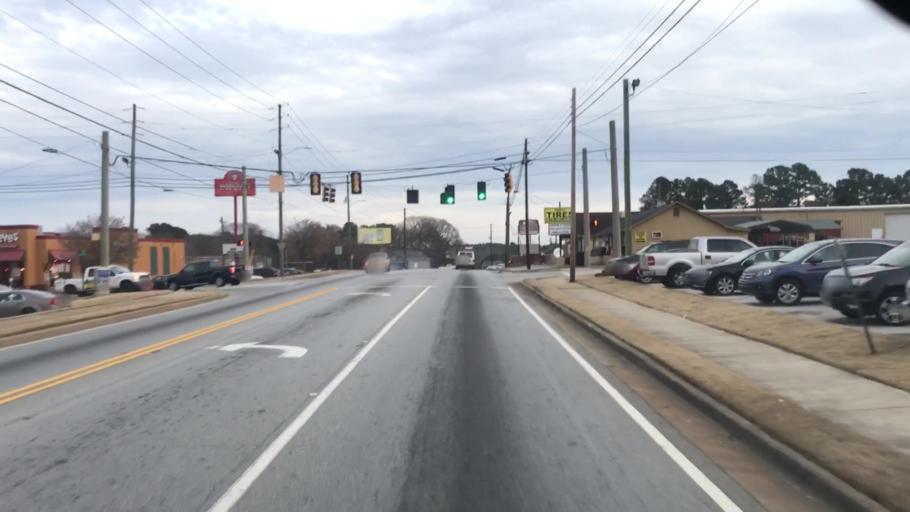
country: US
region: Georgia
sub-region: Barrow County
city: Winder
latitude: 33.9872
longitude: -83.7170
